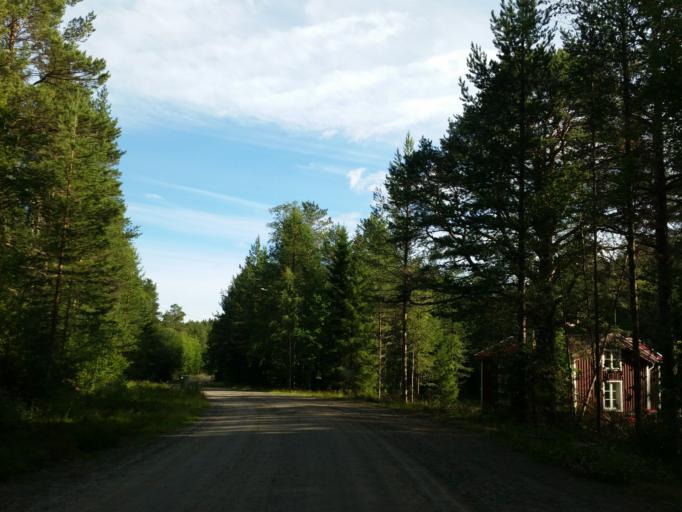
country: SE
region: Vaesterbotten
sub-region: Robertsfors Kommun
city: Robertsfors
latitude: 64.0401
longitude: 20.8499
